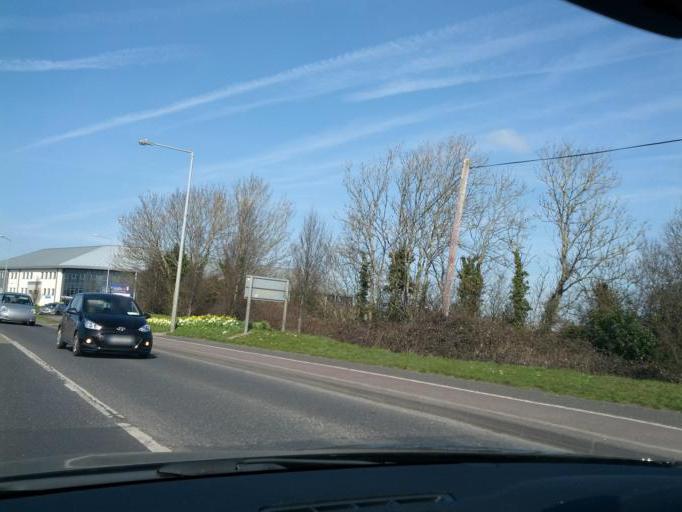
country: IE
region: Leinster
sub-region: Kildare
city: Celbridge
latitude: 53.3568
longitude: -6.5478
